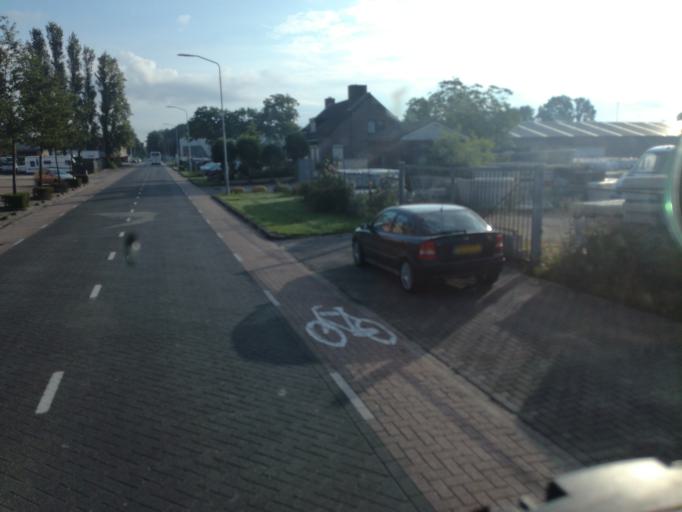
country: NL
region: North Brabant
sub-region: Gemeente Goirle
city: Goirle
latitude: 51.5135
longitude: 5.0526
